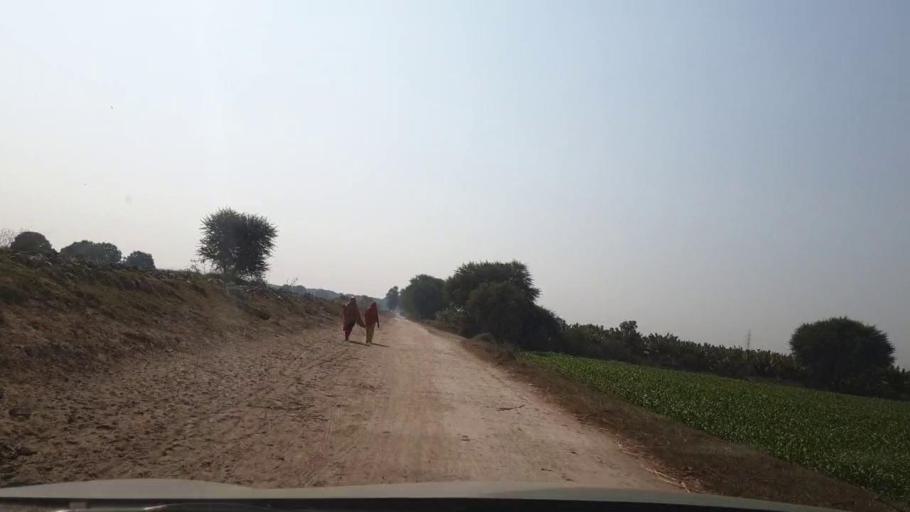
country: PK
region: Sindh
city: Tando Allahyar
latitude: 25.5034
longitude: 68.7860
